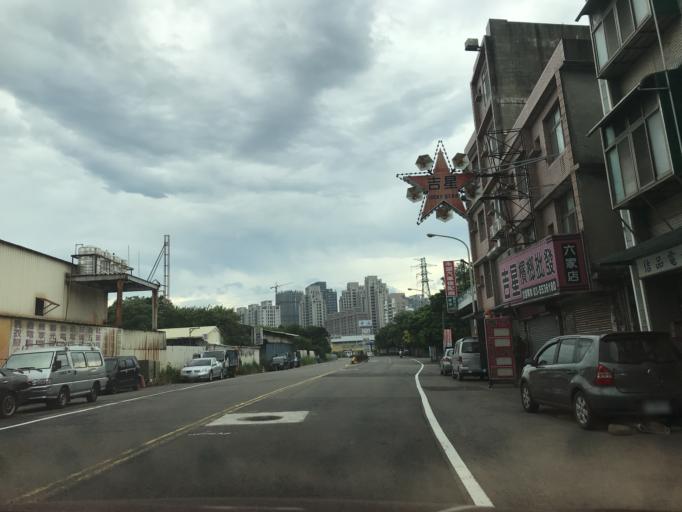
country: TW
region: Taiwan
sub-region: Hsinchu
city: Zhubei
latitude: 24.8184
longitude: 121.0315
